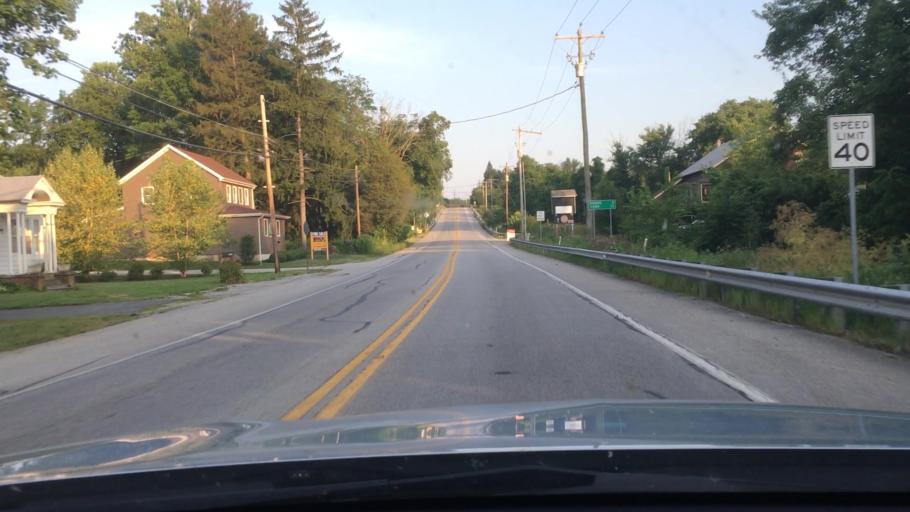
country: US
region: Pennsylvania
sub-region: York County
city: Dover
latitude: 40.0635
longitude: -76.9178
